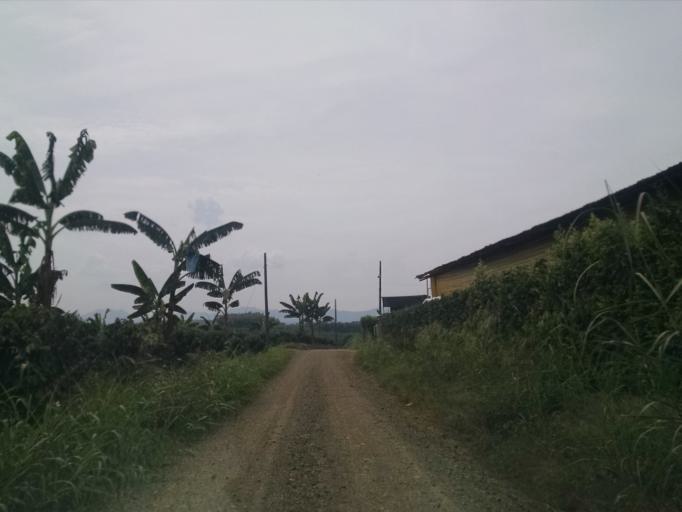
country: CO
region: Valle del Cauca
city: Ulloa
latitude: 4.7123
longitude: -75.7541
